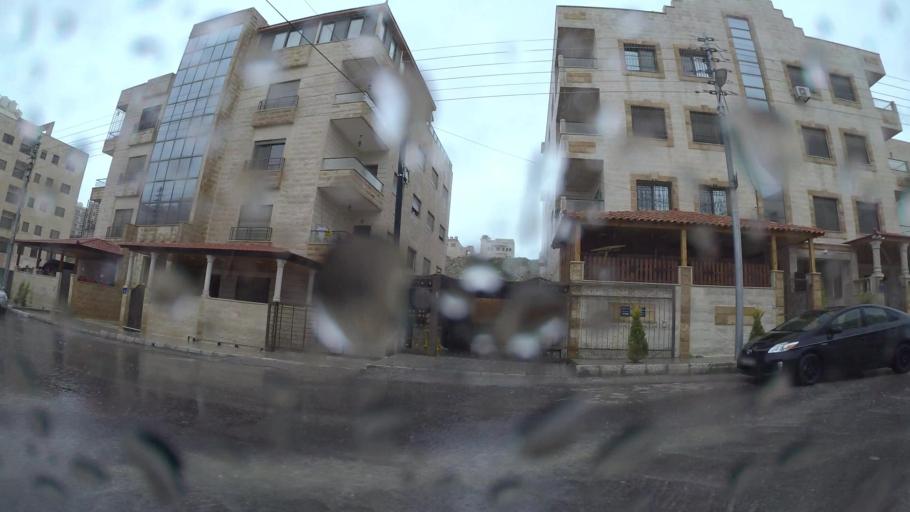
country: JO
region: Amman
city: Al Jubayhah
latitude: 32.0236
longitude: 35.8908
